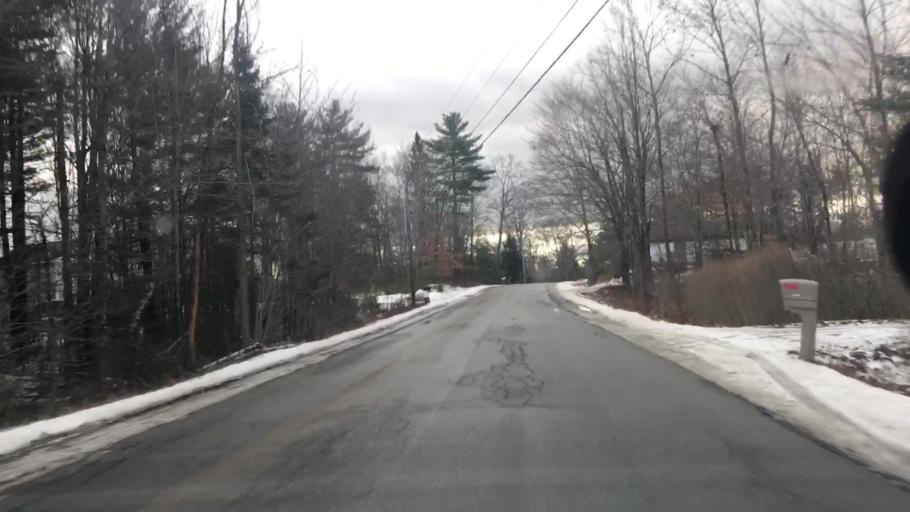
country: US
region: Maine
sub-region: Hancock County
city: Dedham
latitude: 44.6391
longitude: -68.7045
